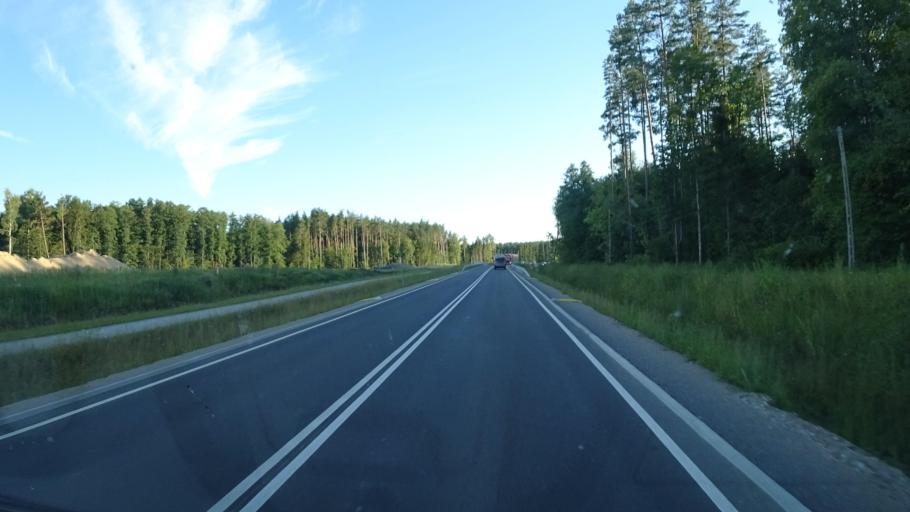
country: PL
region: Warmian-Masurian Voivodeship
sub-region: Powiat elcki
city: Elk
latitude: 53.8469
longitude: 22.4562
